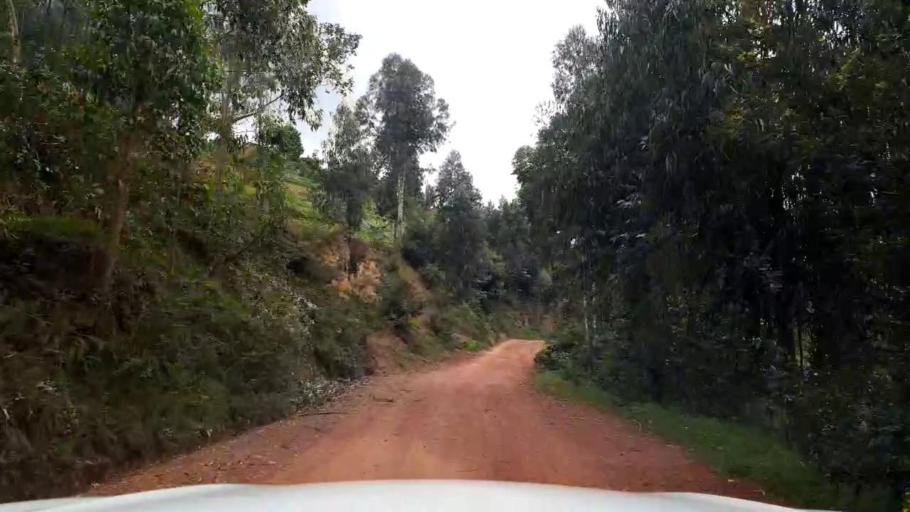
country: RW
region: Northern Province
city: Byumba
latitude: -1.4867
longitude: 29.9271
